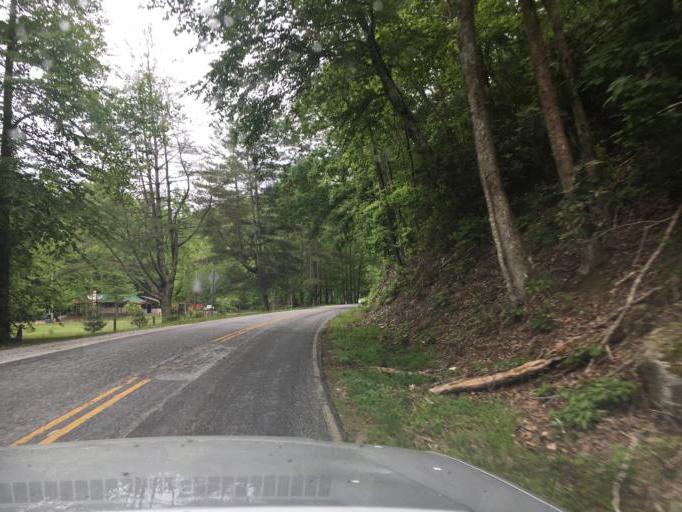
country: US
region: South Carolina
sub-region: Greenville County
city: Tigerville
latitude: 35.1294
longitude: -82.3811
